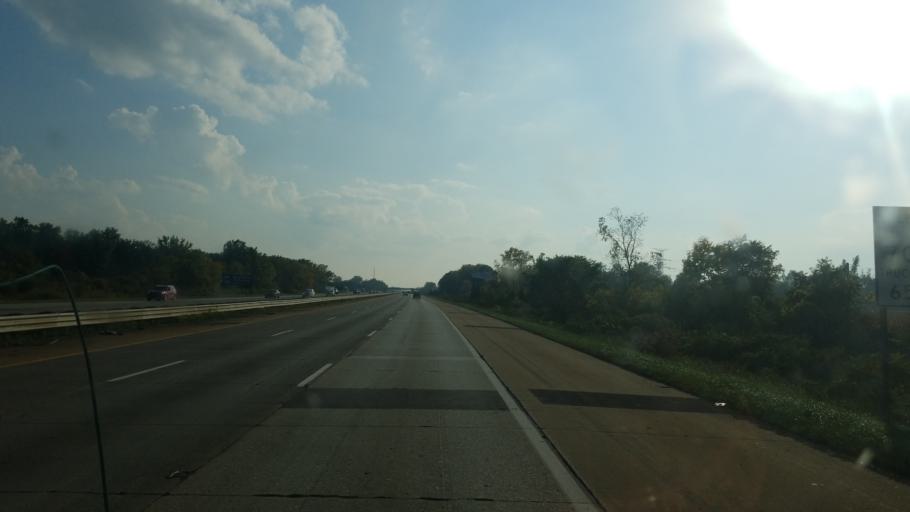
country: US
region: Michigan
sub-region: Monroe County
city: South Monroe
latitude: 41.8704
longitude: -83.4019
